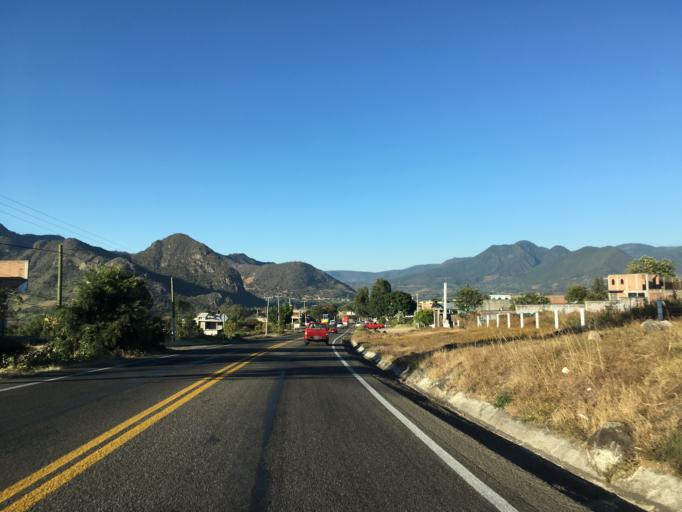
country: MX
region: Michoacan
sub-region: Tuxpan
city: La Soledad
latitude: 19.5374
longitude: -100.4757
